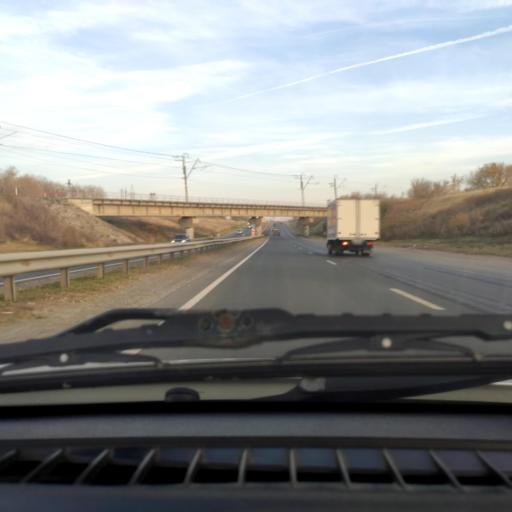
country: RU
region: Samara
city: Tol'yatti
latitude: 53.5692
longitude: 49.4806
